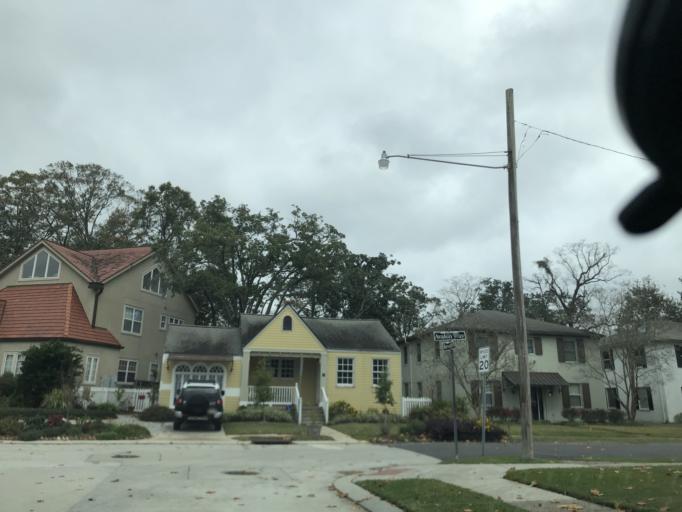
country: US
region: Louisiana
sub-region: Jefferson Parish
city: Metairie
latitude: 29.9809
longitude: -90.1501
